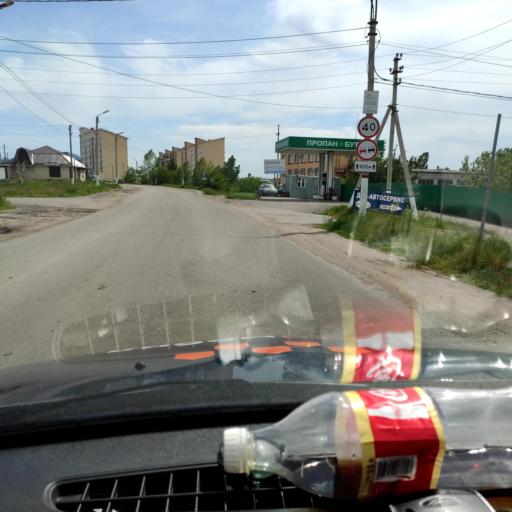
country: RU
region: Voronezj
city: Novaya Usman'
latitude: 51.6105
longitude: 39.3881
